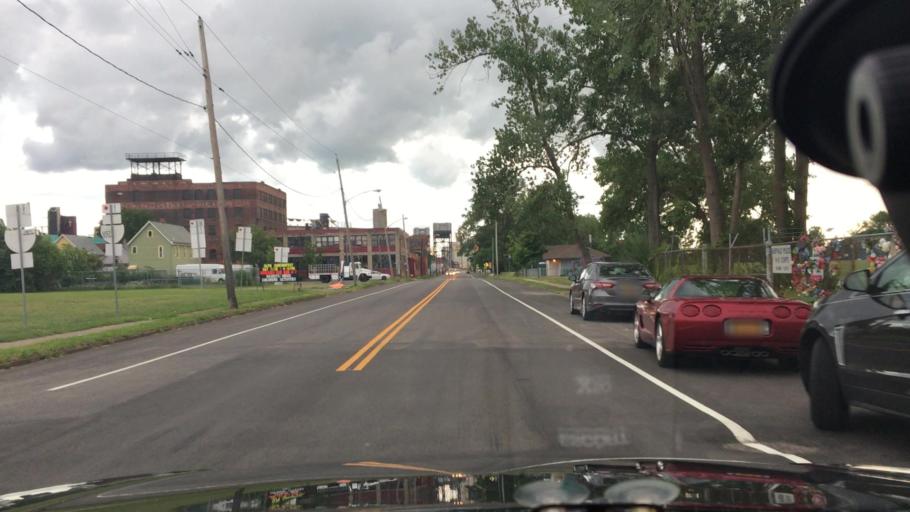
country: US
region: New York
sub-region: Erie County
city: Buffalo
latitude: 42.8697
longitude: -78.8653
